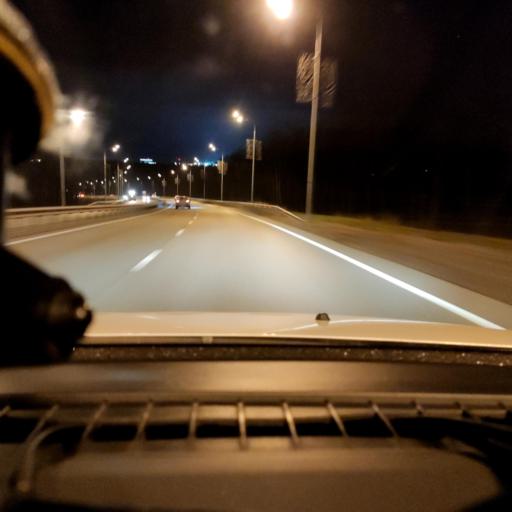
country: RU
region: Samara
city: Novosemeykino
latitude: 53.3151
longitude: 50.2303
